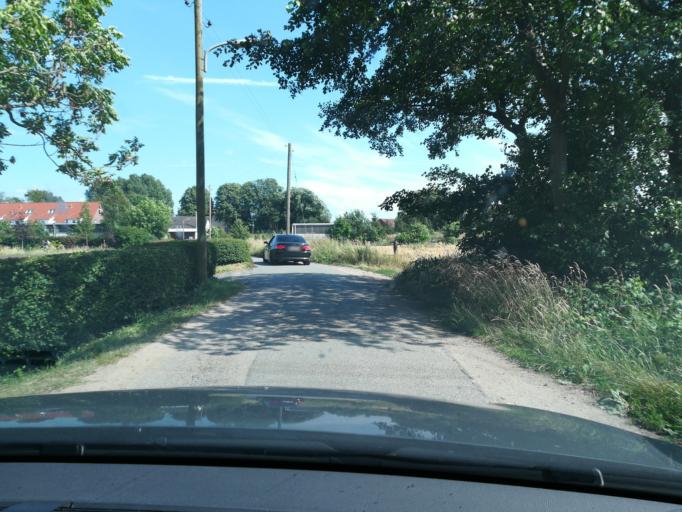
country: DE
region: Hamburg
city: Rothenburgsort
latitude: 53.4905
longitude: 10.0454
